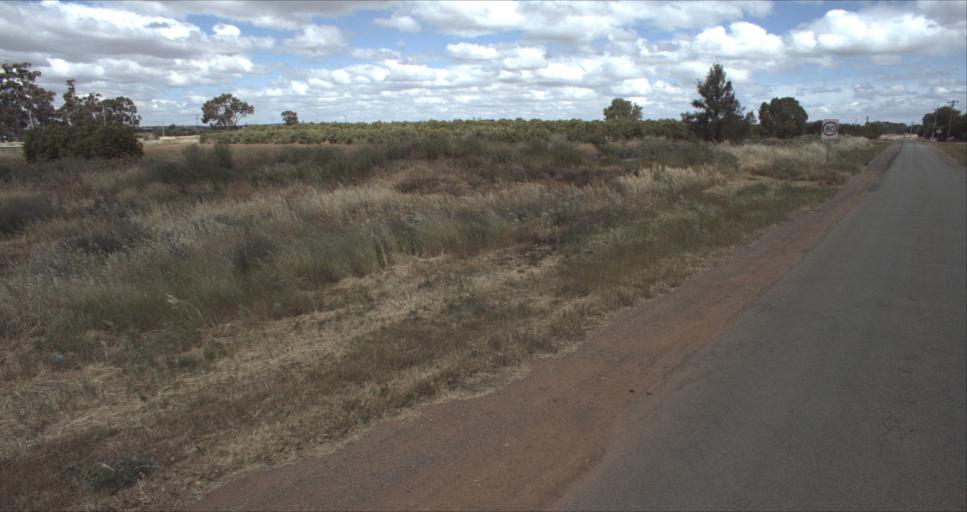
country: AU
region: New South Wales
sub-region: Leeton
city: Leeton
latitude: -34.5792
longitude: 146.3972
